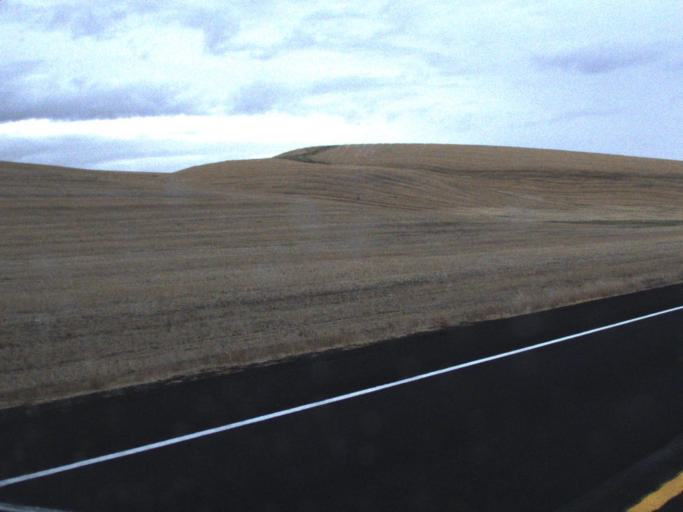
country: US
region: Washington
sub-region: Garfield County
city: Pomeroy
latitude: 46.8032
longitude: -117.7639
